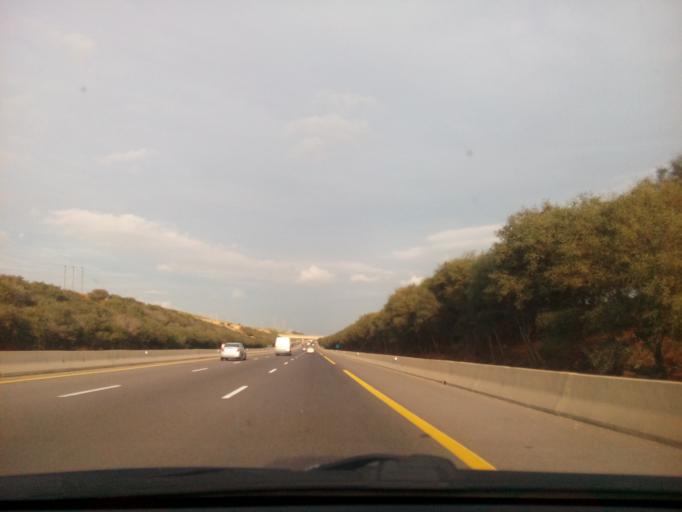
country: DZ
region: Relizane
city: Relizane
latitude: 35.7453
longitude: 0.3453
